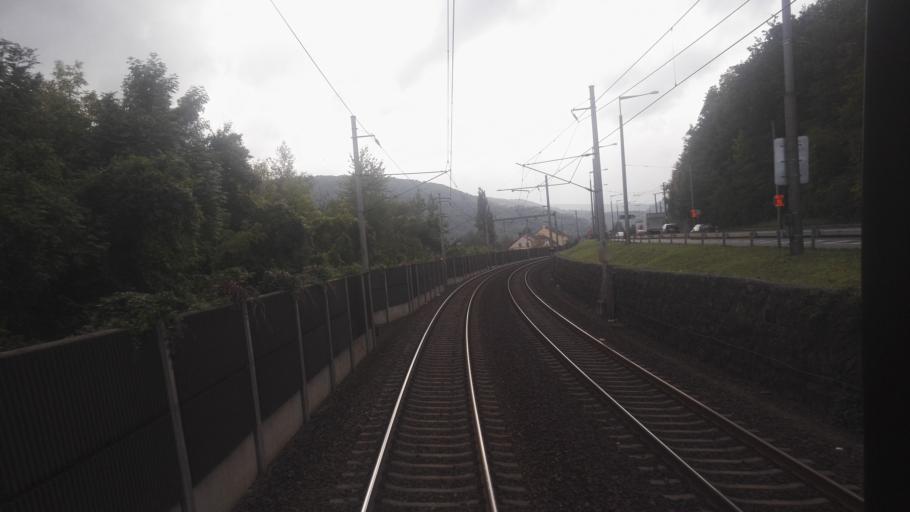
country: CZ
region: Ustecky
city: Velke Brezno
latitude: 50.6681
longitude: 14.1024
